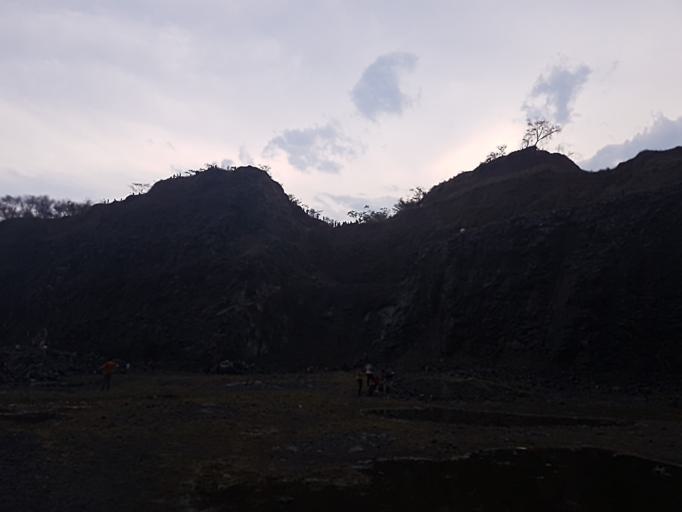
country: PY
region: Central
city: Nemby
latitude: -25.4034
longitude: -57.5359
